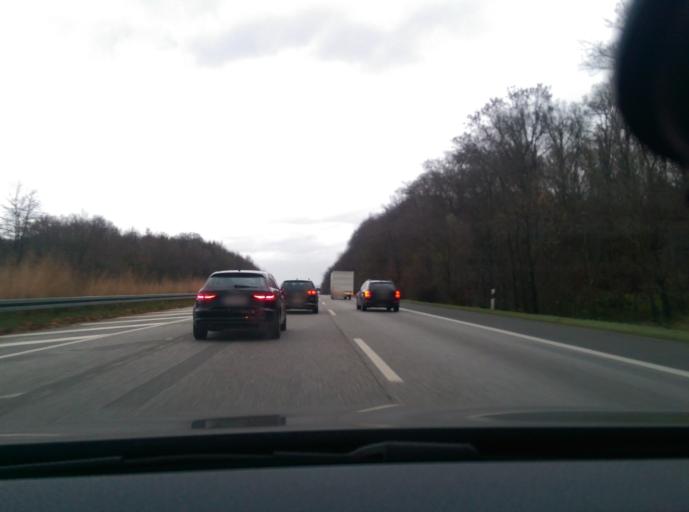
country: DE
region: Lower Saxony
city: Hillerse
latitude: 51.6702
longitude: 9.9215
